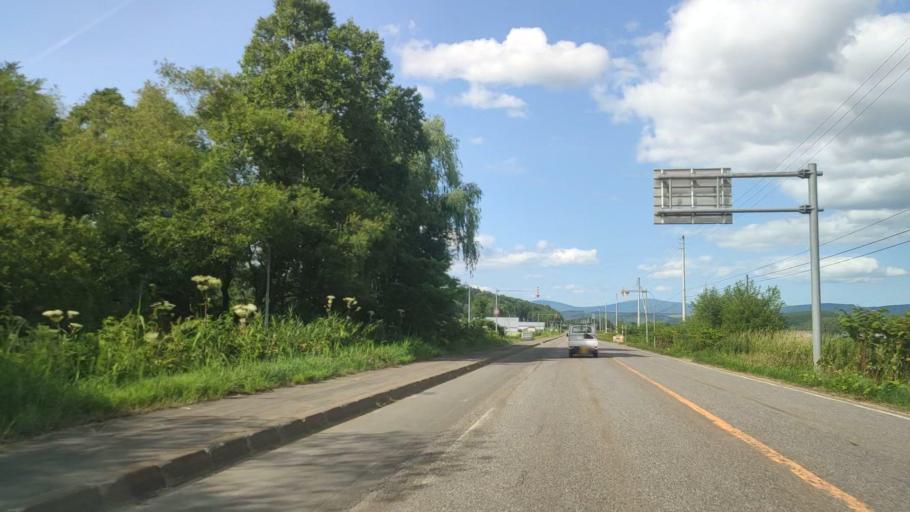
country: JP
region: Hokkaido
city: Nayoro
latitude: 44.3981
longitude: 142.3950
